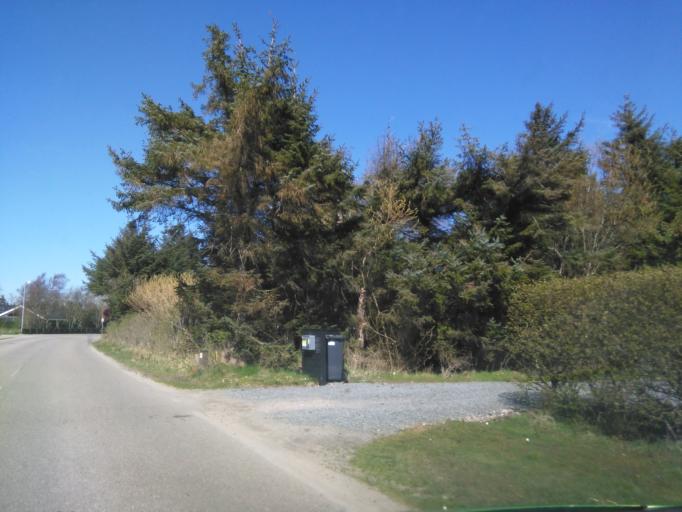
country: DK
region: South Denmark
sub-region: Varde Kommune
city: Oksbol
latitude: 55.5494
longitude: 8.1343
